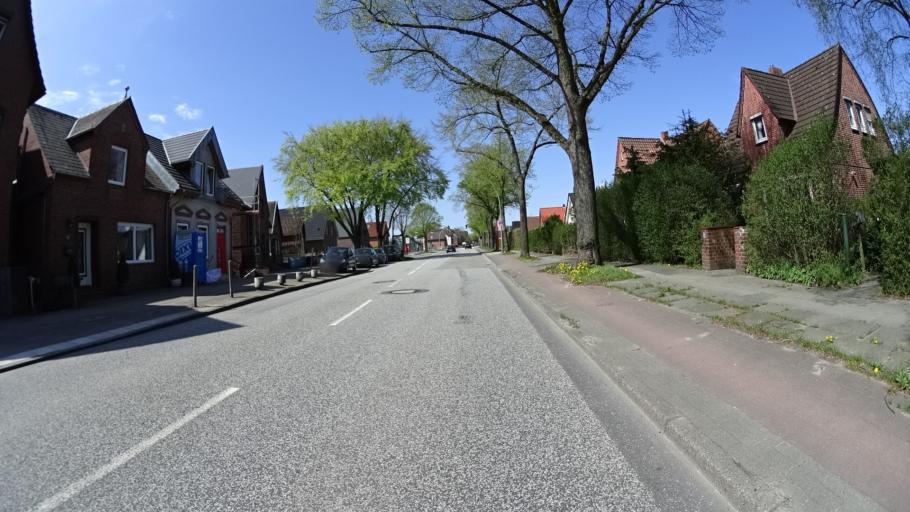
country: DE
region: Hamburg
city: Altona
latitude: 53.5355
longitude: 9.8547
